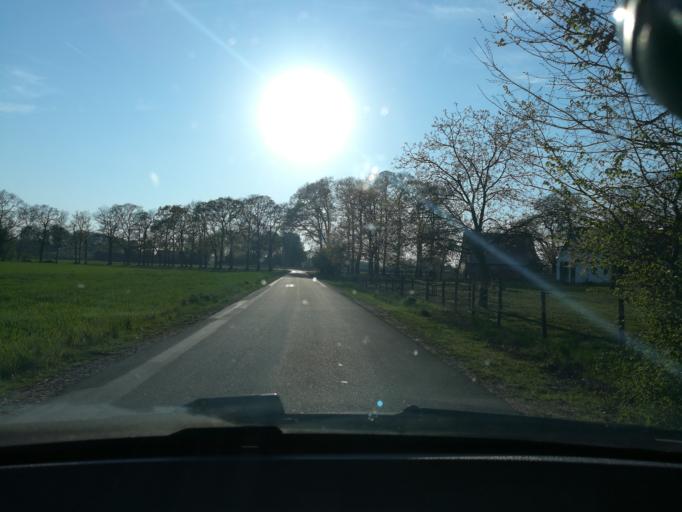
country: DE
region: North Rhine-Westphalia
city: Versmold
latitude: 52.0207
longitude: 8.1078
